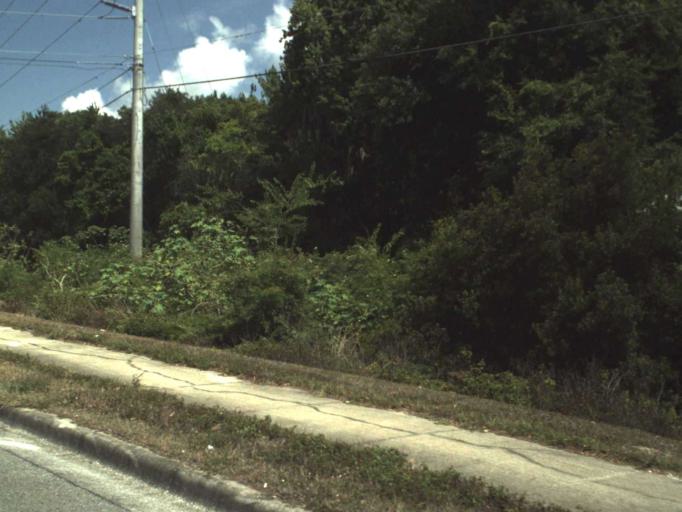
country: US
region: Florida
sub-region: Lake County
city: Tavares
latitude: 28.8147
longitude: -81.7571
